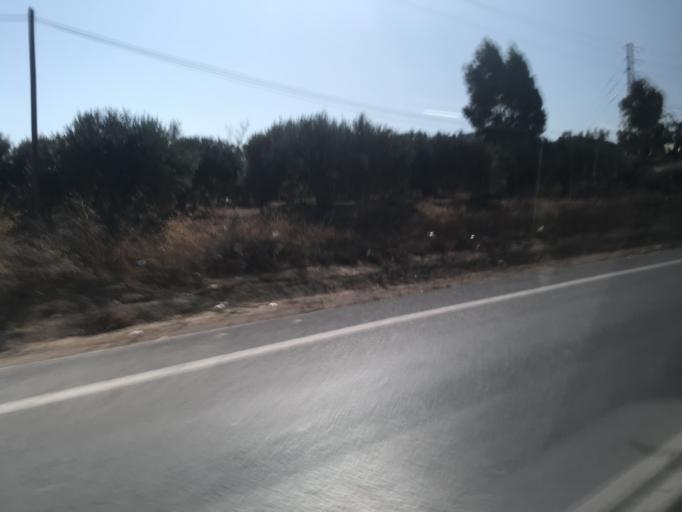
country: GR
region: Crete
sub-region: Nomos Irakleiou
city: Gazi
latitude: 35.3095
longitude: 25.0908
